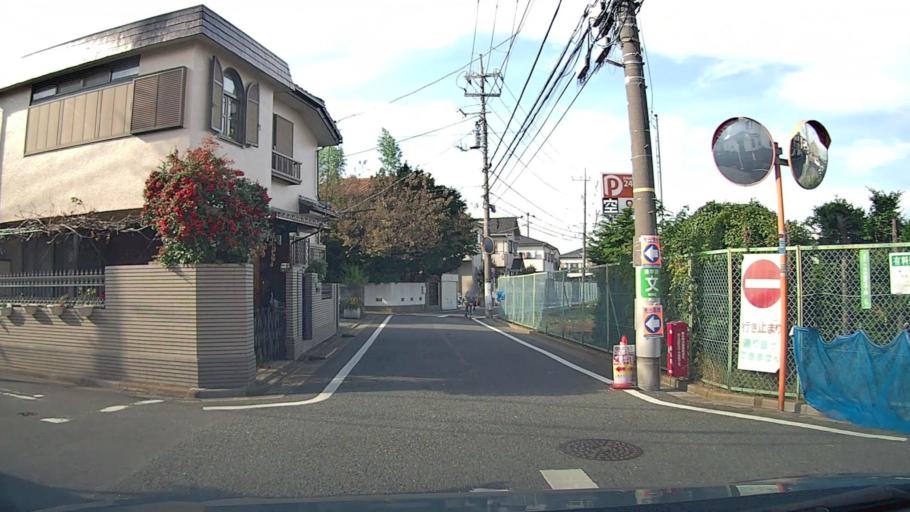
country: JP
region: Saitama
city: Asaka
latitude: 35.7620
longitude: 139.5837
